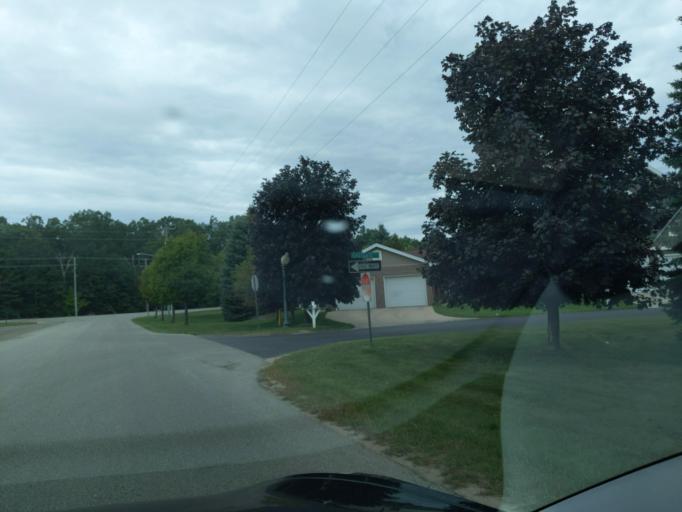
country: US
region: Michigan
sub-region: Grand Traverse County
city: Traverse City
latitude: 44.7534
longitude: -85.5786
